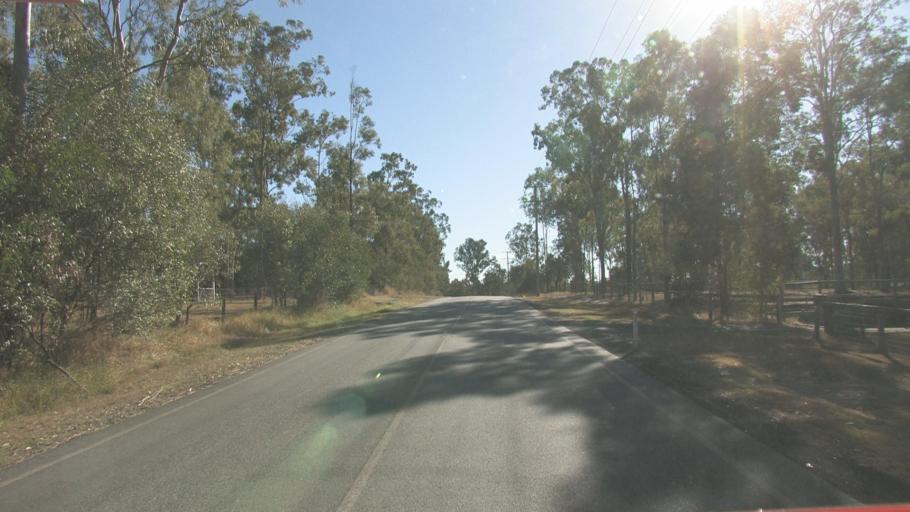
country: AU
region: Queensland
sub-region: Logan
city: North Maclean
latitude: -27.8163
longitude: 152.9885
